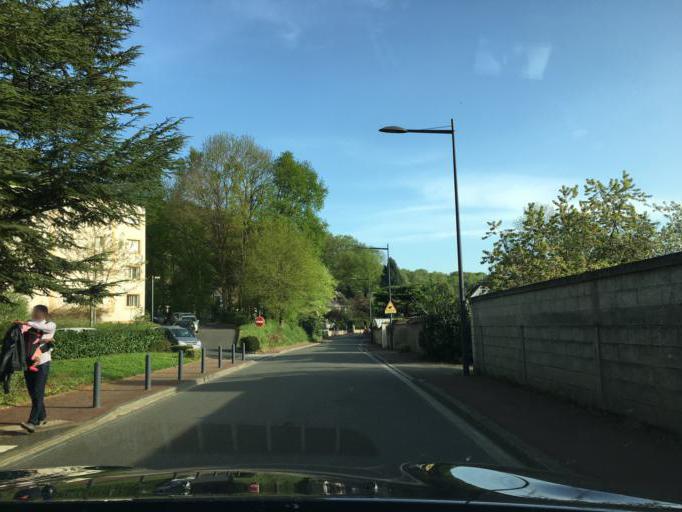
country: FR
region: Centre
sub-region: Departement d'Eure-et-Loir
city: Epernon
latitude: 48.6132
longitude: 1.6712
